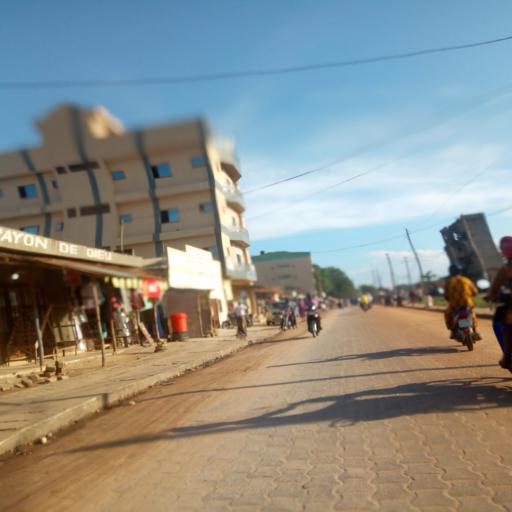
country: BJ
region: Atlantique
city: Hevie
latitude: 6.3923
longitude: 2.2720
